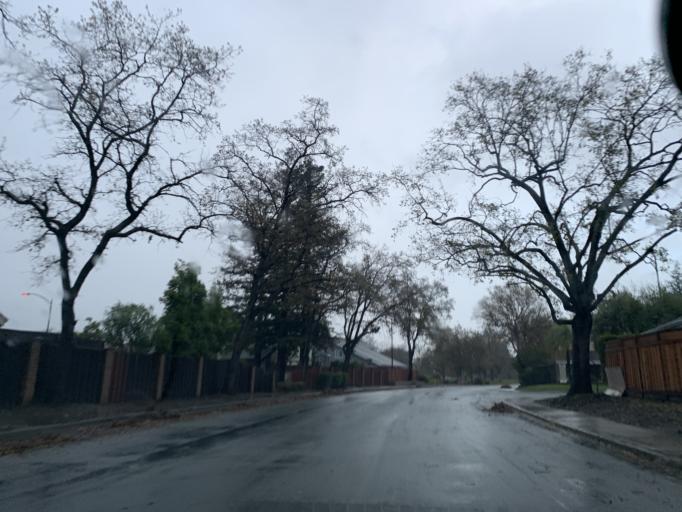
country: US
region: California
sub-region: Santa Clara County
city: Cambrian Park
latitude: 37.2567
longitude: -121.9451
